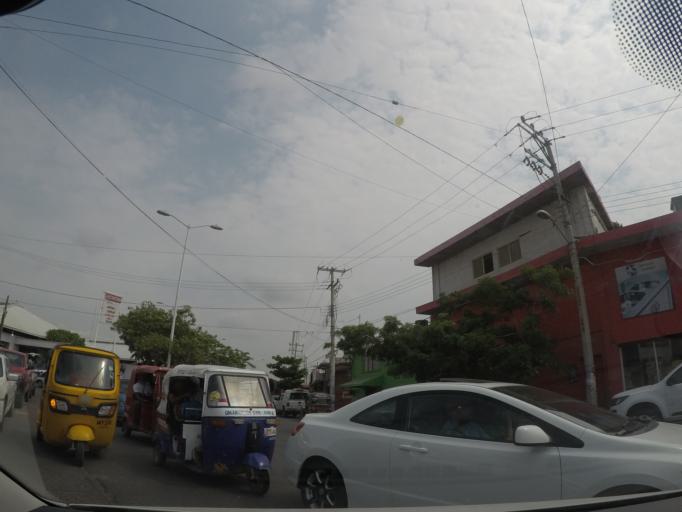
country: MX
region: Oaxaca
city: Juchitan de Zaragoza
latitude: 16.4447
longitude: -95.0245
